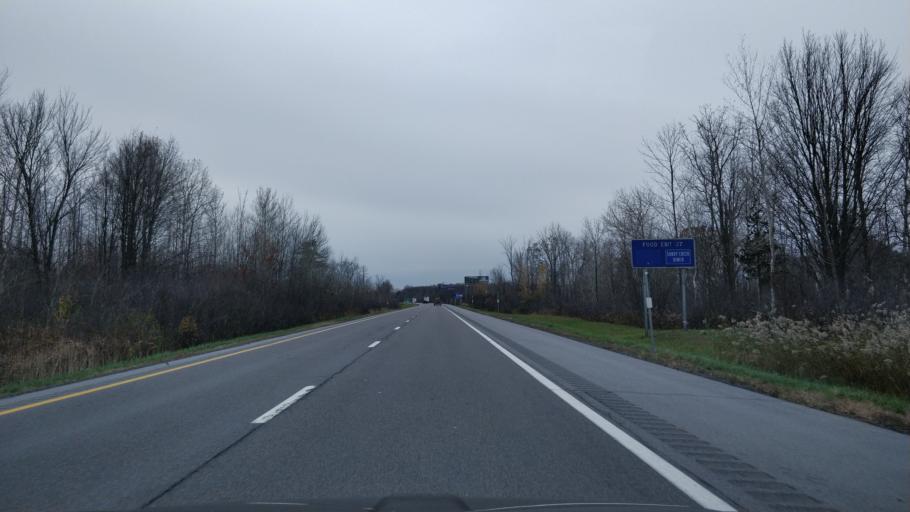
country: US
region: New York
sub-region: Oswego County
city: Pulaski
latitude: 43.6578
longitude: -76.0762
